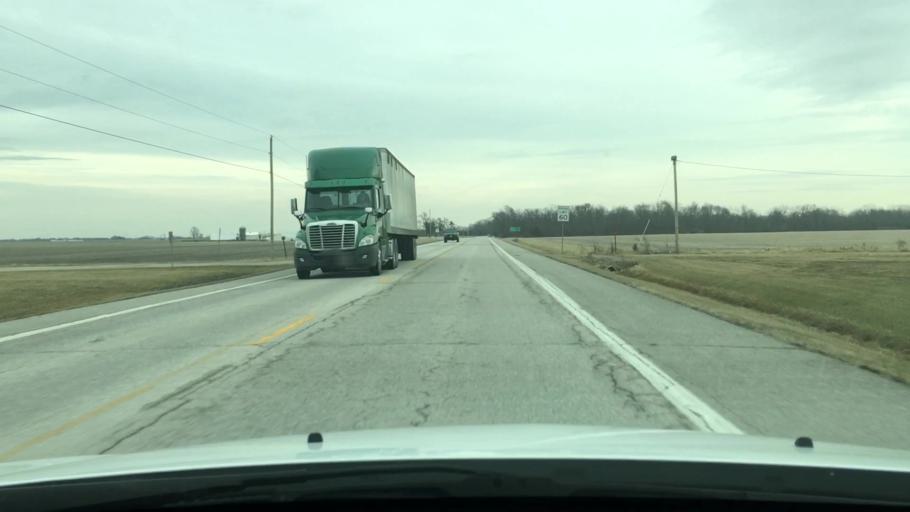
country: US
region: Missouri
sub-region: Audrain County
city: Vandalia
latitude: 39.2792
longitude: -91.5724
